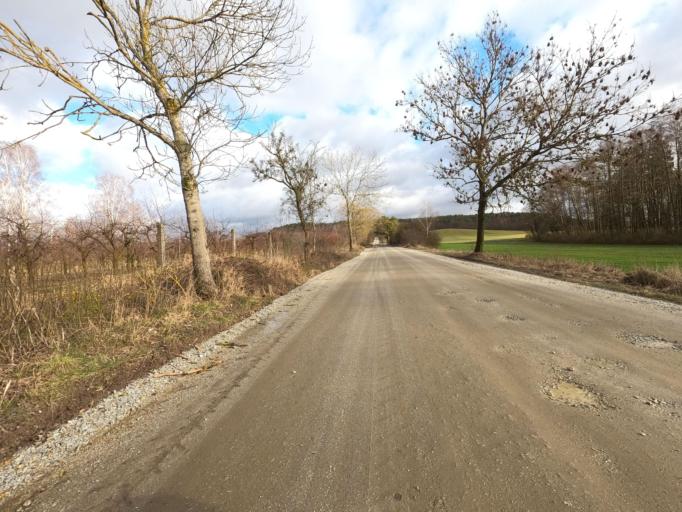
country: PL
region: Greater Poland Voivodeship
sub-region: Powiat pilski
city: Miasteczko Krajenskie
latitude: 53.1020
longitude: 17.0394
